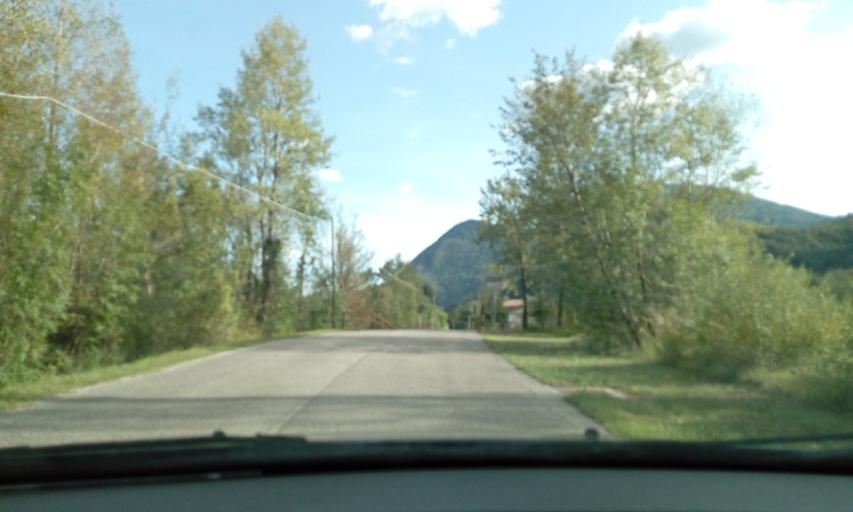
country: IT
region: Friuli Venezia Giulia
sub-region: Provincia di Udine
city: Trasaghis
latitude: 46.3116
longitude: 13.0511
